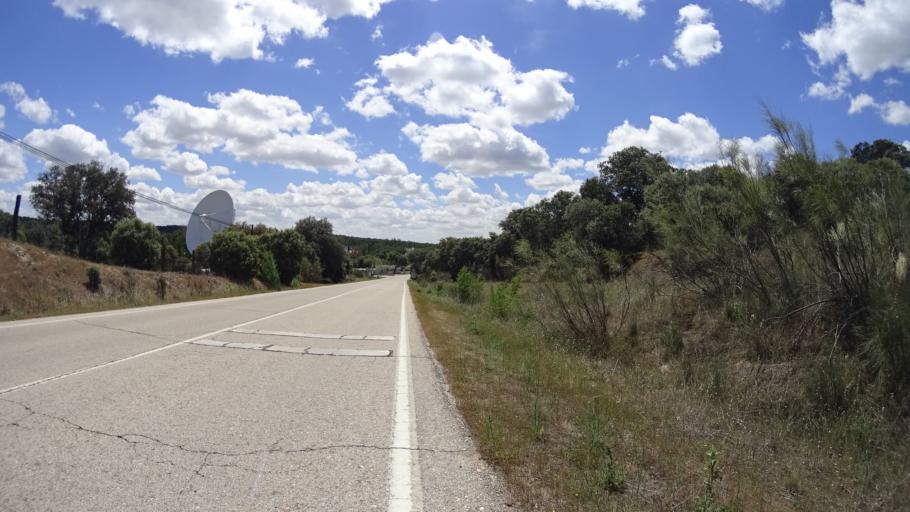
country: ES
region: Madrid
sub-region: Provincia de Madrid
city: Villanueva del Pardillo
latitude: 40.4462
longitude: -3.9534
